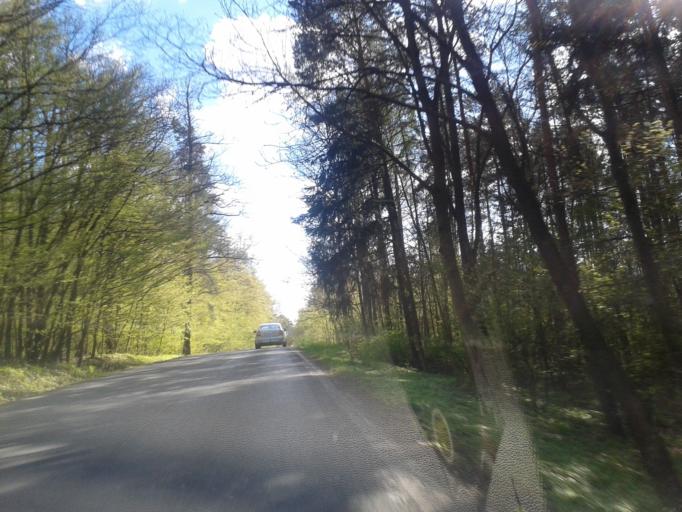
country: CZ
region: Central Bohemia
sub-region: Okres Beroun
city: Beroun
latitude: 49.9945
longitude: 14.0912
